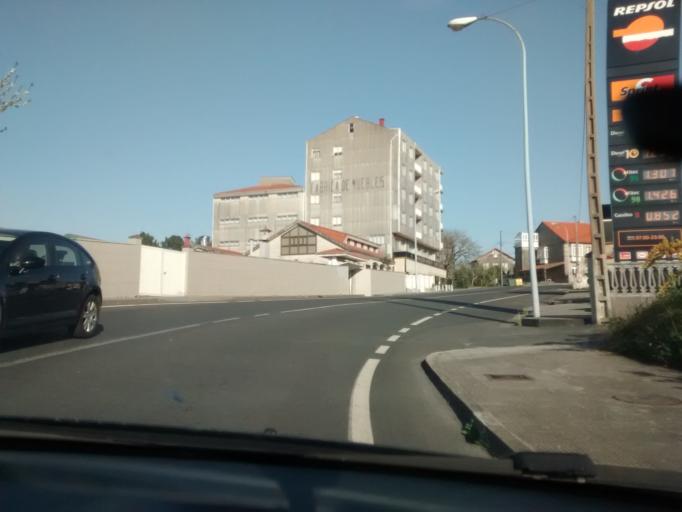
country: ES
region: Galicia
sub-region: Provincia de Pontevedra
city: A Estrada
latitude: 42.6941
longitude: -8.4921
